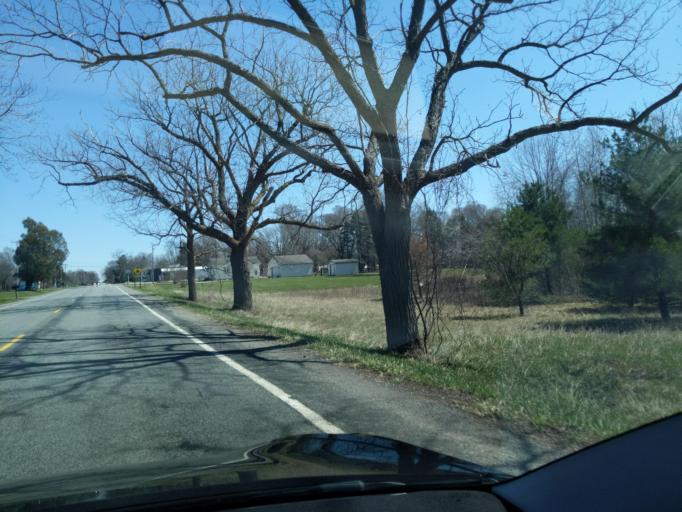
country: US
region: Michigan
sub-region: Ingham County
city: Holt
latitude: 42.5821
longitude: -84.5261
